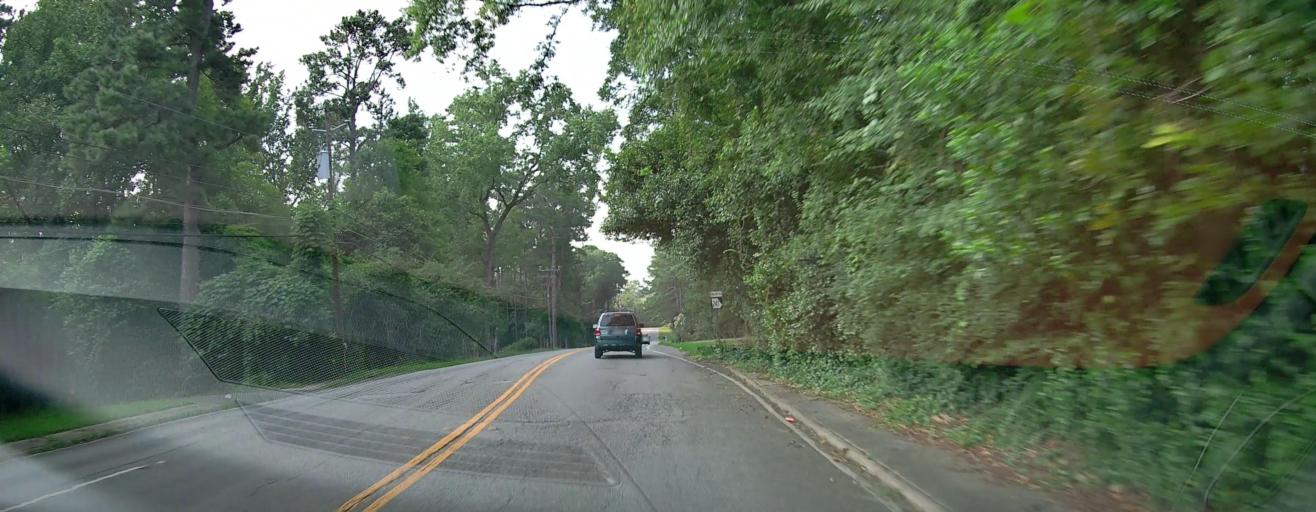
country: US
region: Georgia
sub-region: Bibb County
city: Macon
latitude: 32.8541
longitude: -83.6624
